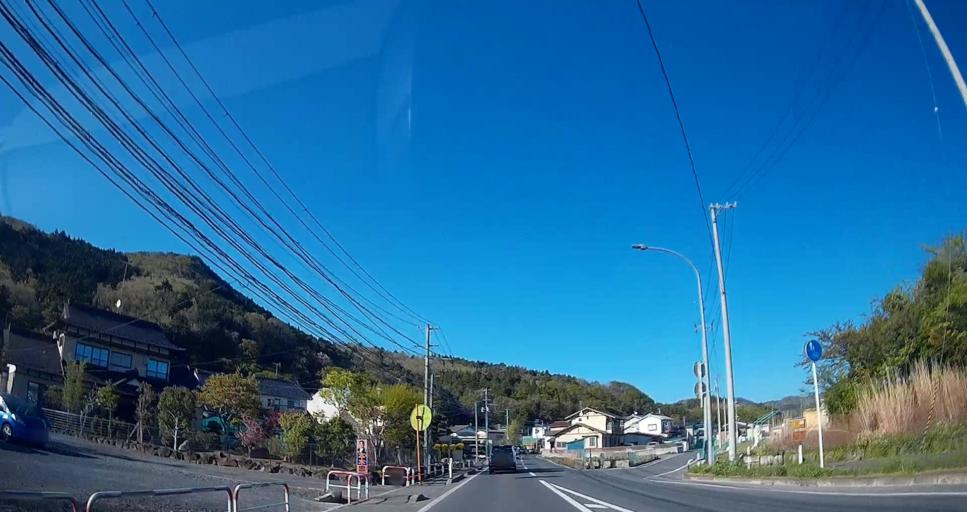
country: JP
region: Miyagi
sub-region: Oshika Gun
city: Onagawa Cho
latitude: 38.4291
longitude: 141.3746
